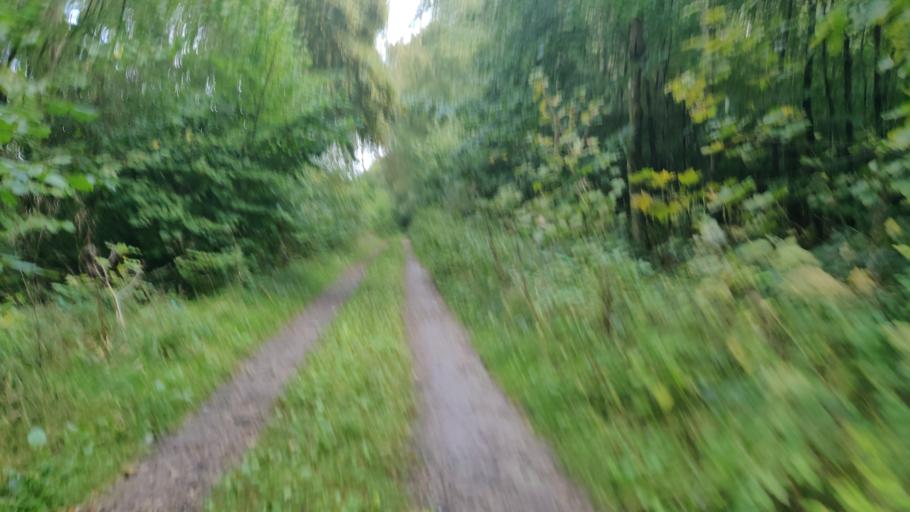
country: DK
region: South Denmark
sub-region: Kolding Kommune
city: Lunderskov
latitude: 55.5451
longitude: 9.3613
